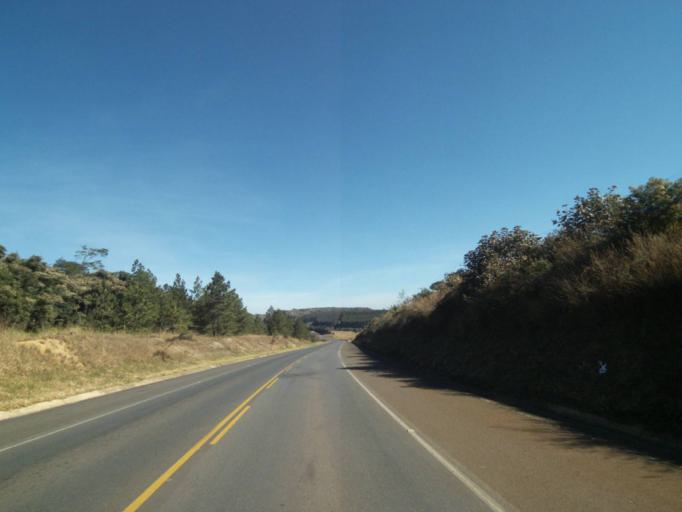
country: BR
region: Parana
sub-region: Tibagi
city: Tibagi
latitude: -24.3979
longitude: -50.3370
